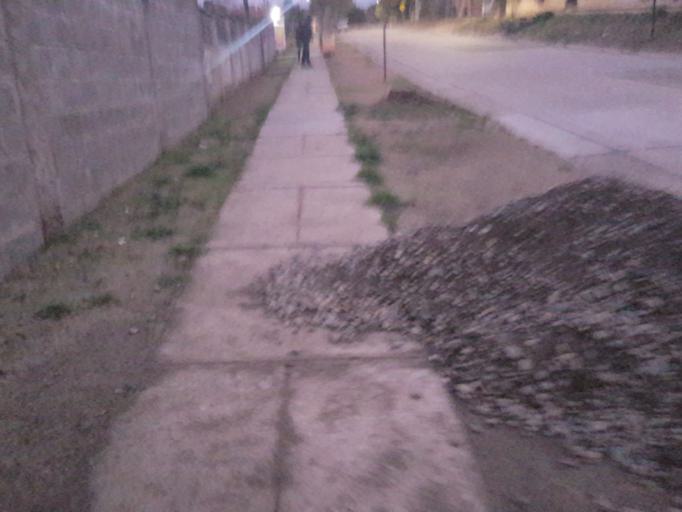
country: CL
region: Valparaiso
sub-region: Provincia de Marga Marga
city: Villa Alemana
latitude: -33.0387
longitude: -71.3494
